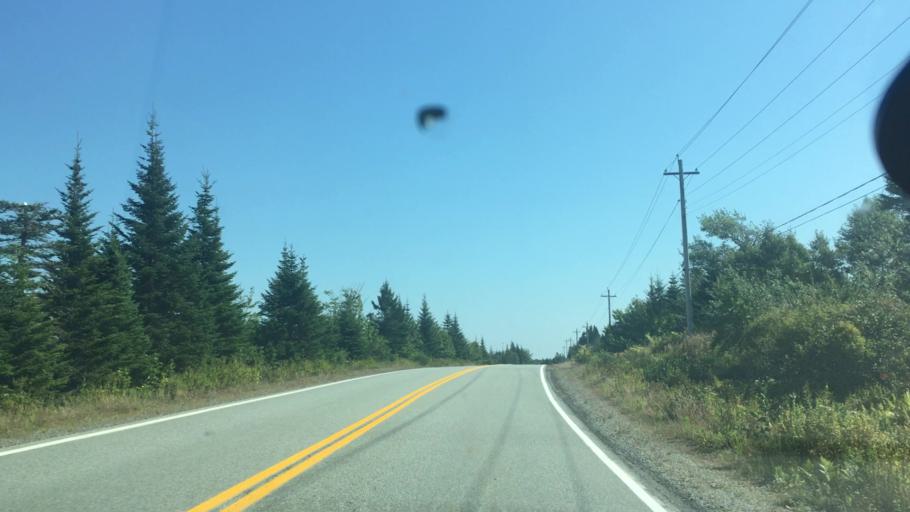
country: CA
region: Nova Scotia
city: Antigonish
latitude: 44.9340
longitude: -62.2809
